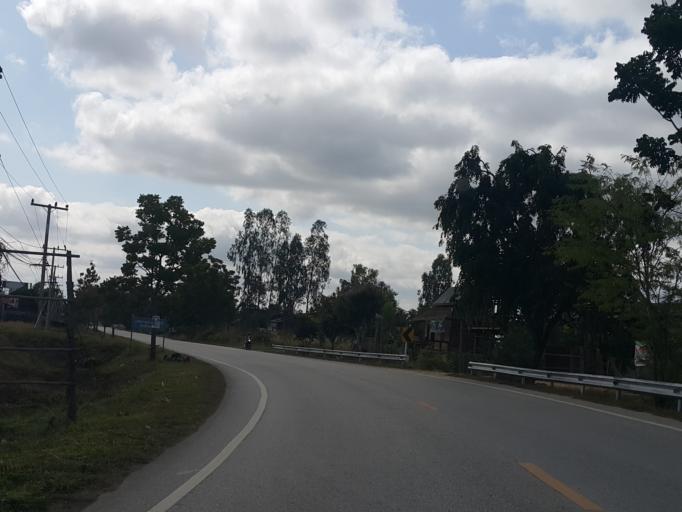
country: TH
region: Lamphun
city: Ban Thi
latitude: 18.6618
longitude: 99.1318
